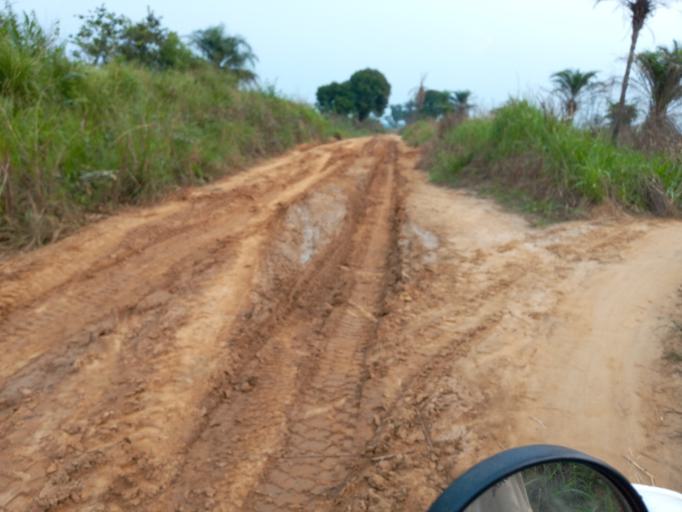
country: CD
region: Bandundu
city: Bandundu
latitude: -3.4945
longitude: 17.6289
